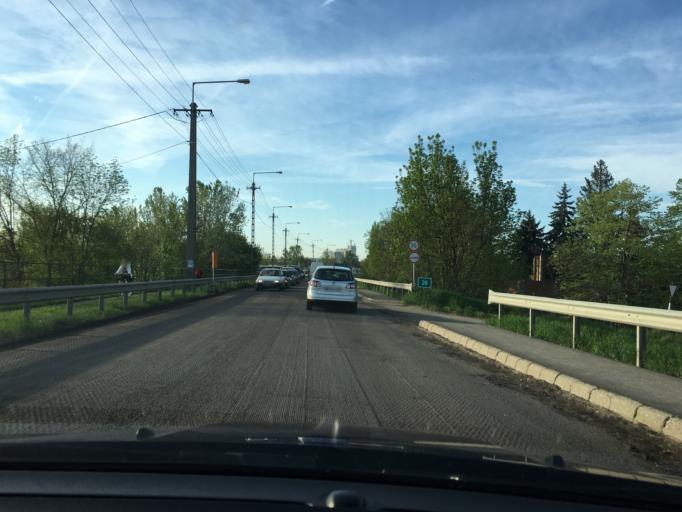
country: HU
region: Hajdu-Bihar
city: Berettyoujfalu
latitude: 47.2081
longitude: 21.5383
